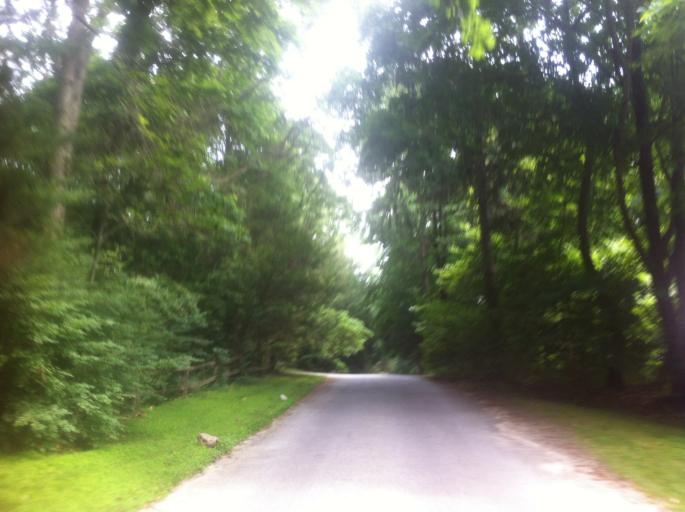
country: US
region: New York
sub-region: Nassau County
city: Locust Valley
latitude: 40.8661
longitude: -73.5818
